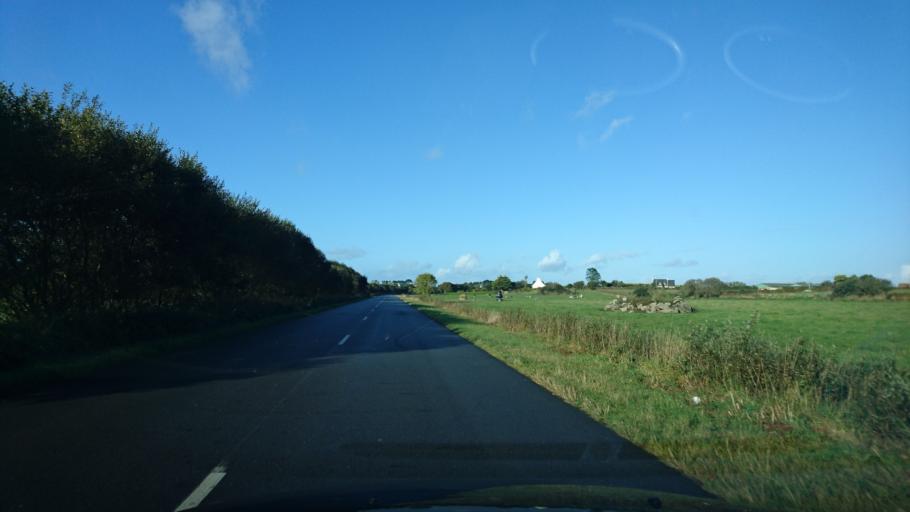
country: FR
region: Brittany
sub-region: Departement du Finistere
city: Plouarzel
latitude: 48.4384
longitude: -4.7253
